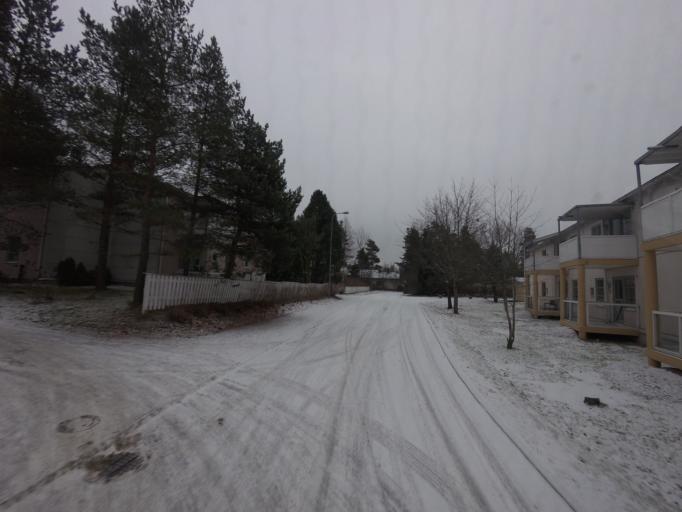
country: FI
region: Uusimaa
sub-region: Helsinki
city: Espoo
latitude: 60.2053
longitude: 24.6269
